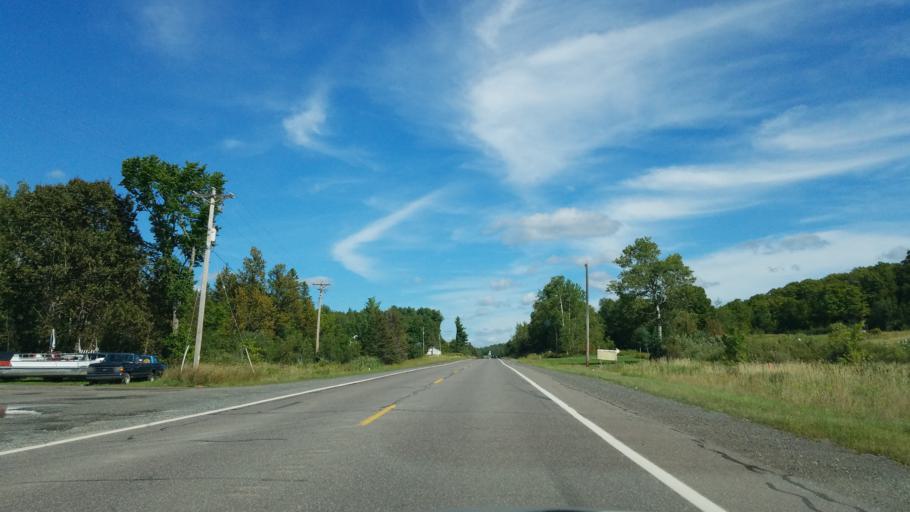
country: US
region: Michigan
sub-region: Baraga County
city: L'Anse
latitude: 46.5451
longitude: -88.5592
